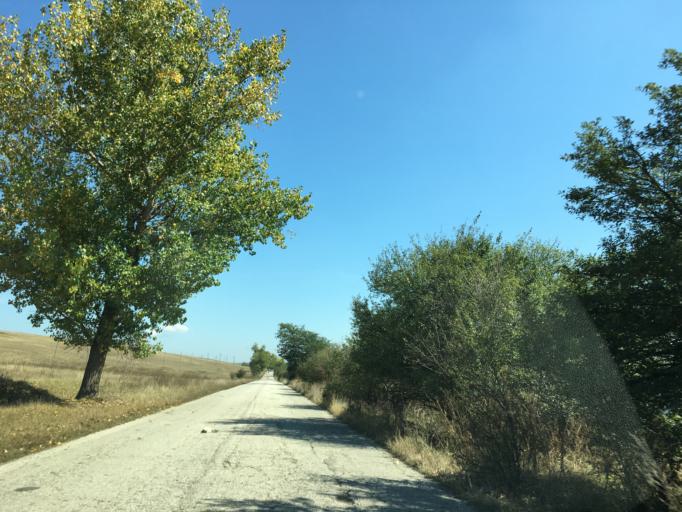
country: BG
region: Pleven
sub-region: Obshtina Knezha
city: Knezha
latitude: 43.5393
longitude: 24.1310
